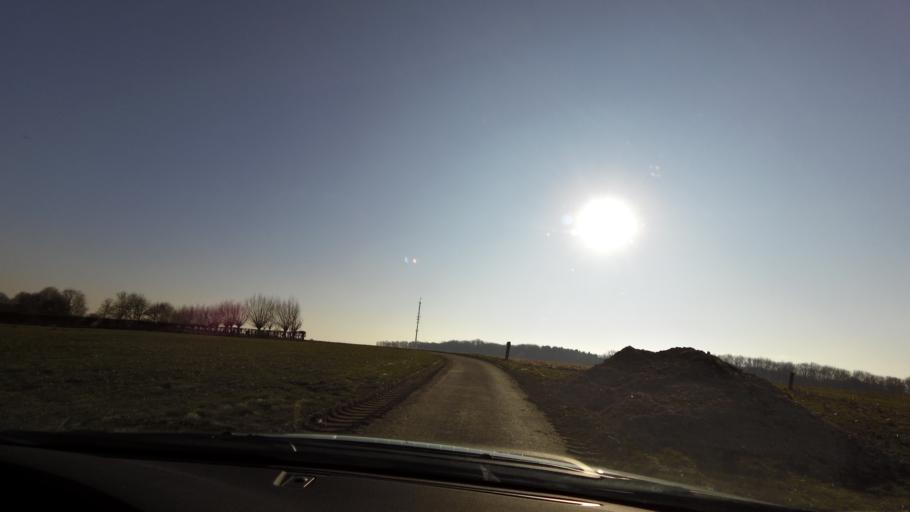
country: NL
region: Limburg
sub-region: Gemeente Voerendaal
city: Ubachsberg
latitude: 50.8347
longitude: 5.9158
